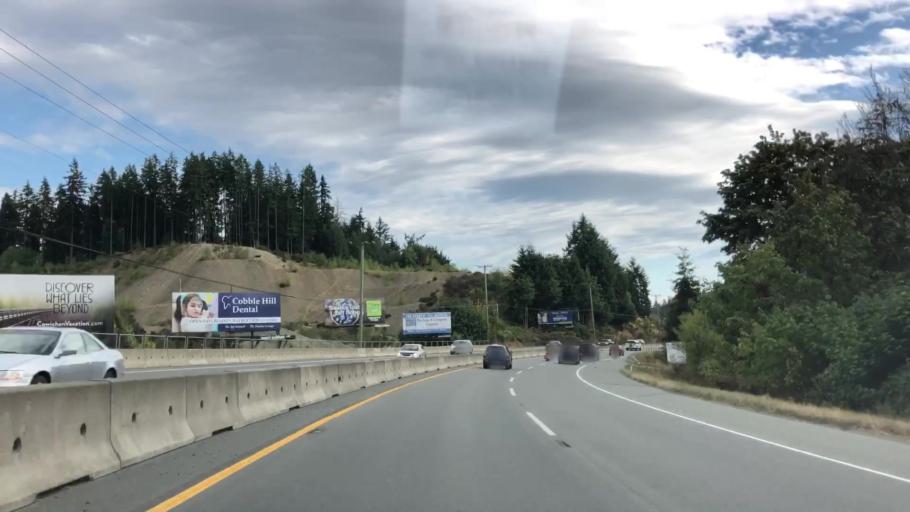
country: CA
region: British Columbia
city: Duncan
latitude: 48.7153
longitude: -123.6101
